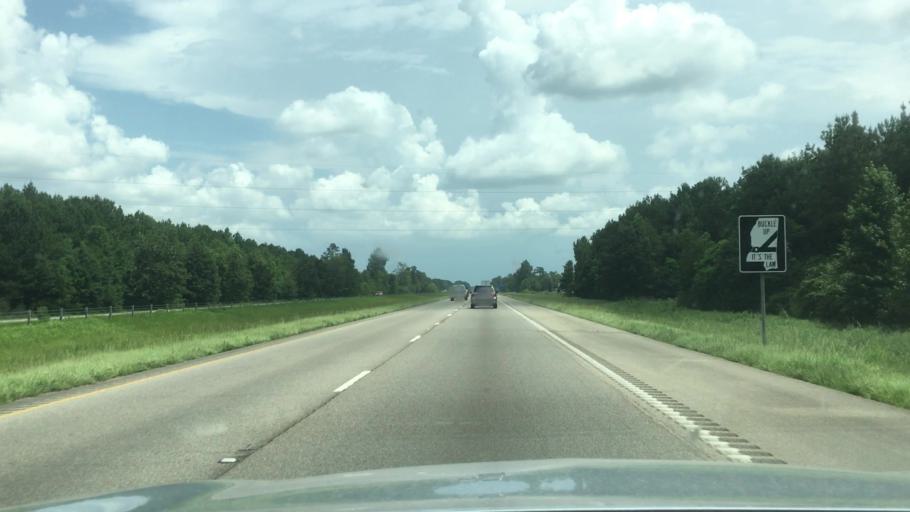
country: US
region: Mississippi
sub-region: Pearl River County
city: Nicholson
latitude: 30.4870
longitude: -89.6736
